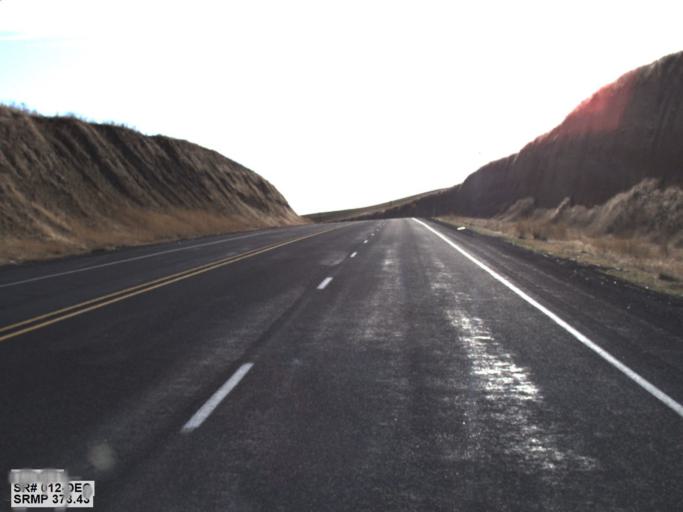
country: US
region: Washington
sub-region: Columbia County
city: Dayton
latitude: 46.3930
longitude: -117.9354
